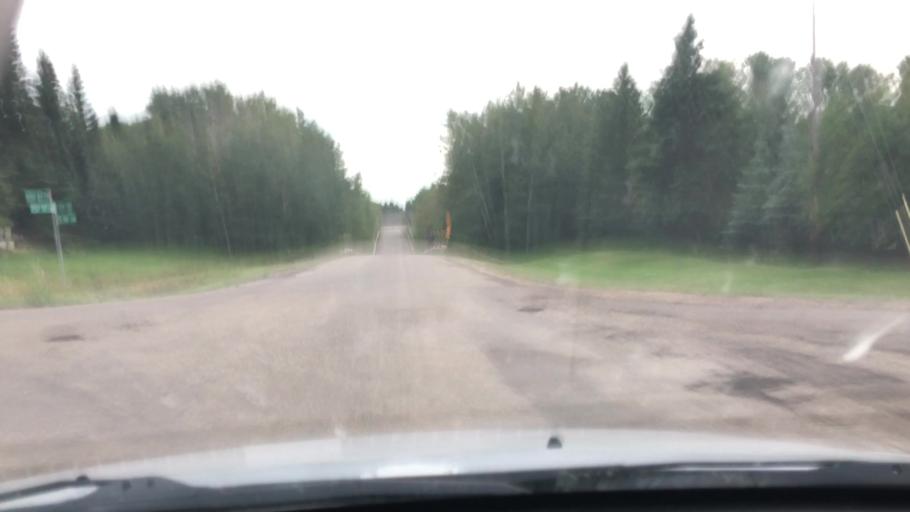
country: CA
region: Alberta
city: Devon
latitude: 53.4286
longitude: -113.6769
